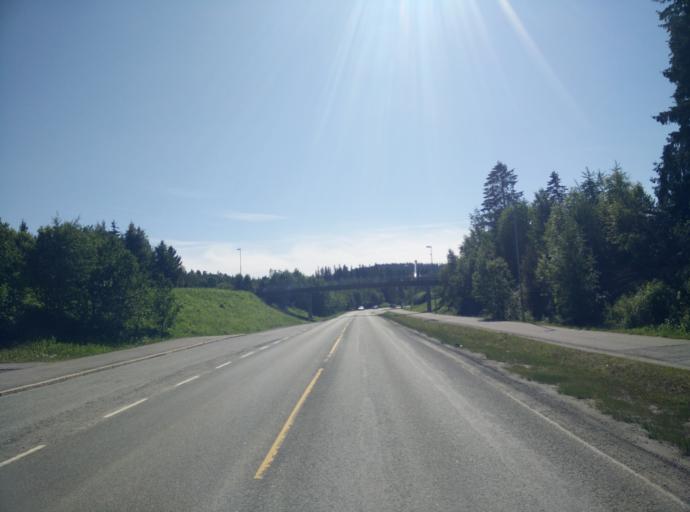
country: NO
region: Sor-Trondelag
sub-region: Trondheim
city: Trondheim
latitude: 63.3850
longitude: 10.3242
